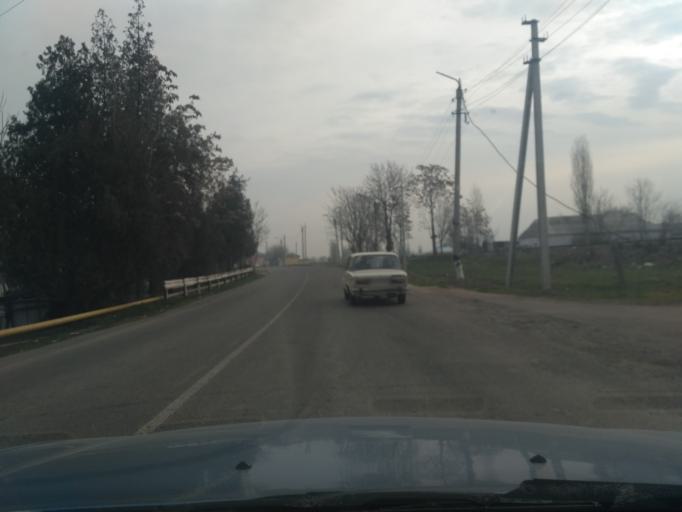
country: UZ
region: Sirdaryo
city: Sirdaryo
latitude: 40.8180
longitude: 68.6657
